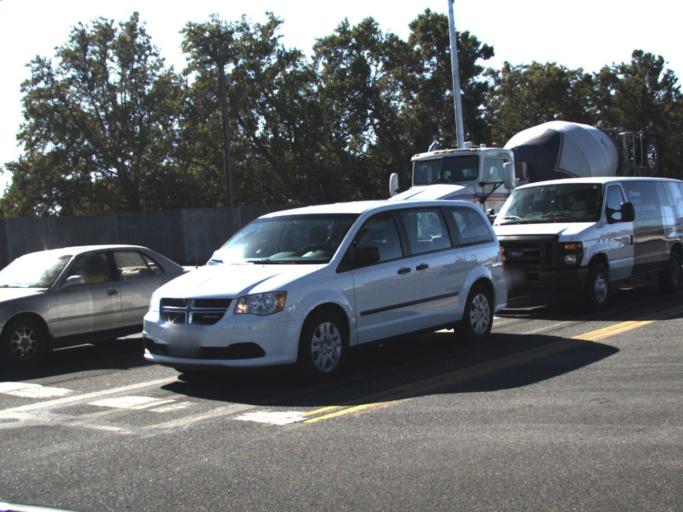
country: US
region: Washington
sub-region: Benton County
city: Richland
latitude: 46.3090
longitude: -119.2864
